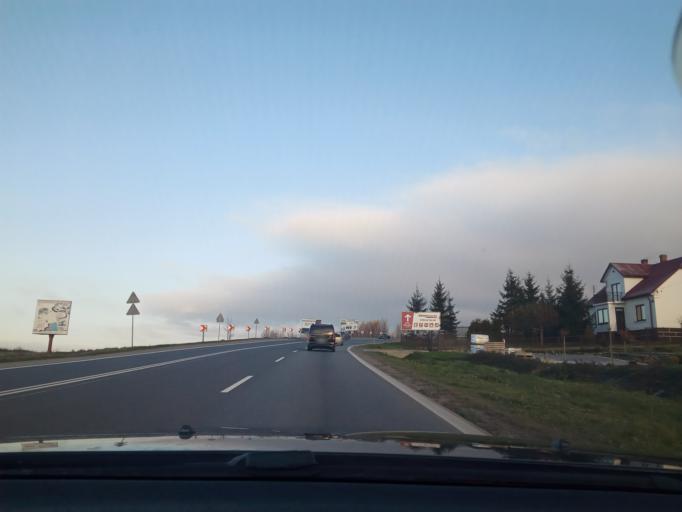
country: PL
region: Lesser Poland Voivodeship
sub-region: Powiat miechowski
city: Miechow
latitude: 50.2957
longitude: 20.0352
